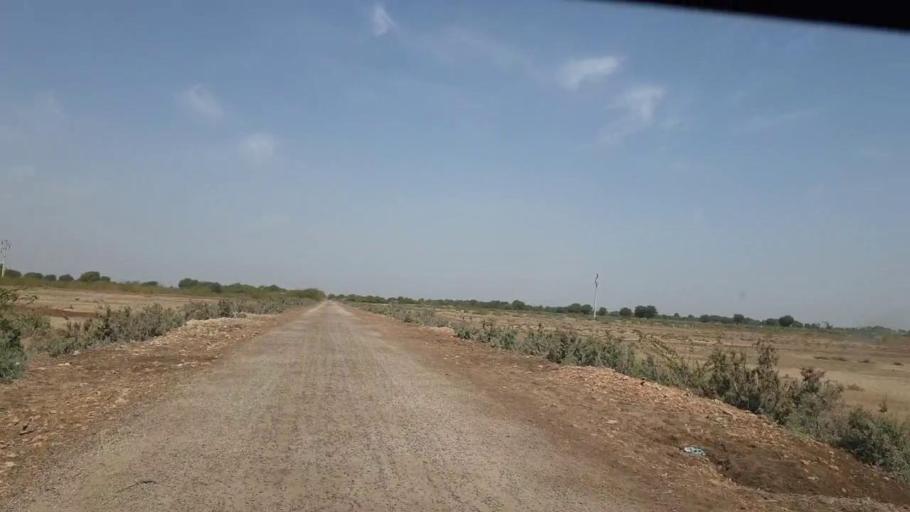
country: PK
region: Sindh
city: Samaro
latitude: 25.2431
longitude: 69.4483
